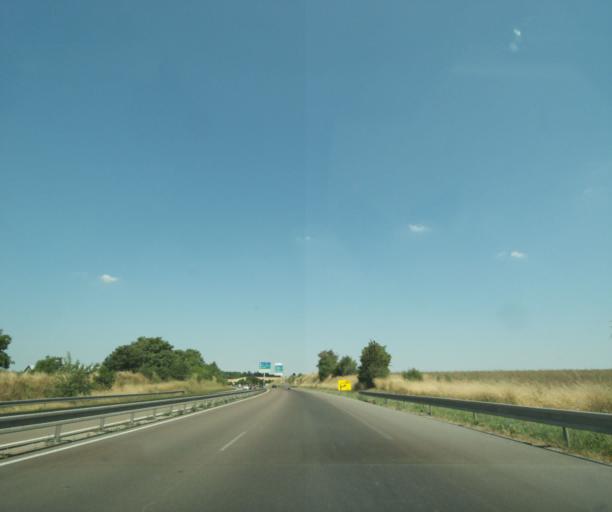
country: FR
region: Champagne-Ardenne
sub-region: Departement de la Marne
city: Saint-Memmie
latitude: 48.9726
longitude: 4.3803
